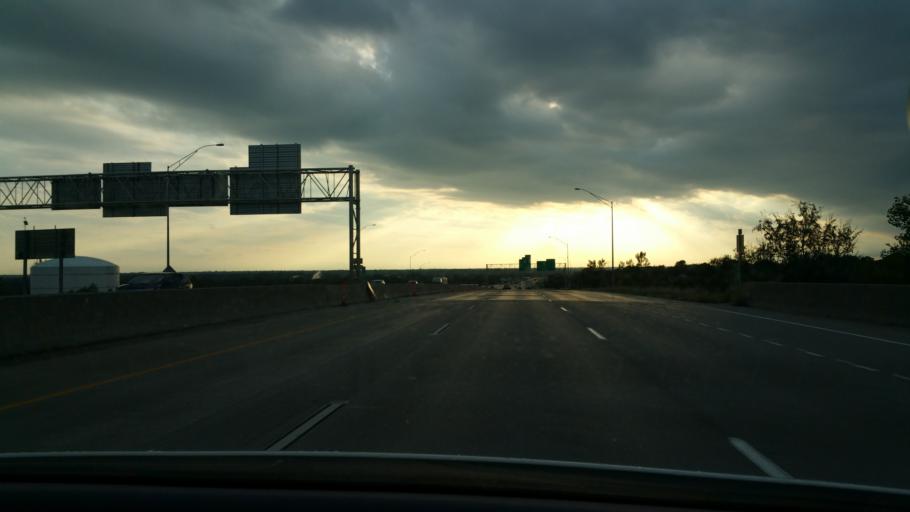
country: US
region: Iowa
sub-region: Polk County
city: Saylorville
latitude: 41.6505
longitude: -93.5906
